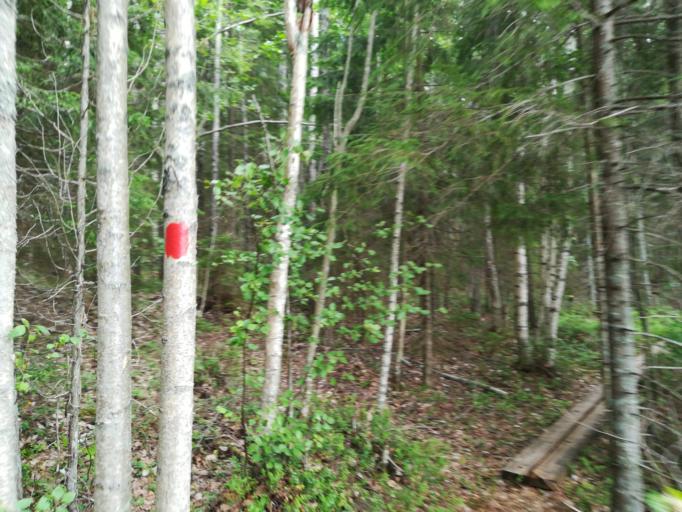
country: FI
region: South Karelia
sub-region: Lappeenranta
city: Savitaipale
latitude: 61.3050
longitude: 27.6143
